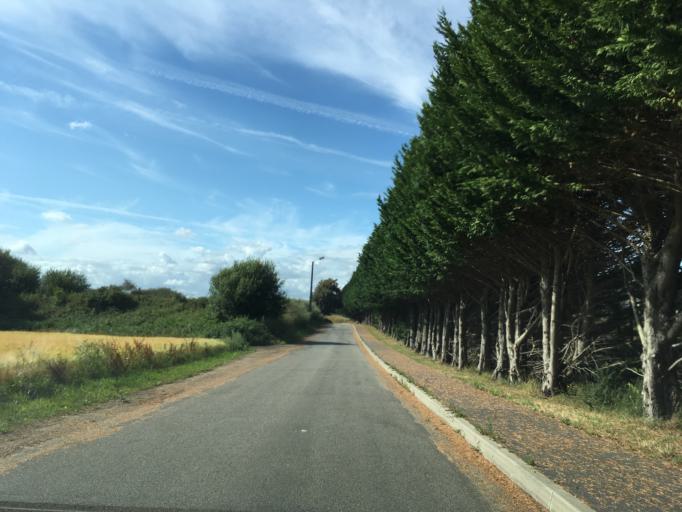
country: FR
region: Brittany
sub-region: Departement du Morbihan
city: Queven
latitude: 47.7623
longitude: -3.4040
